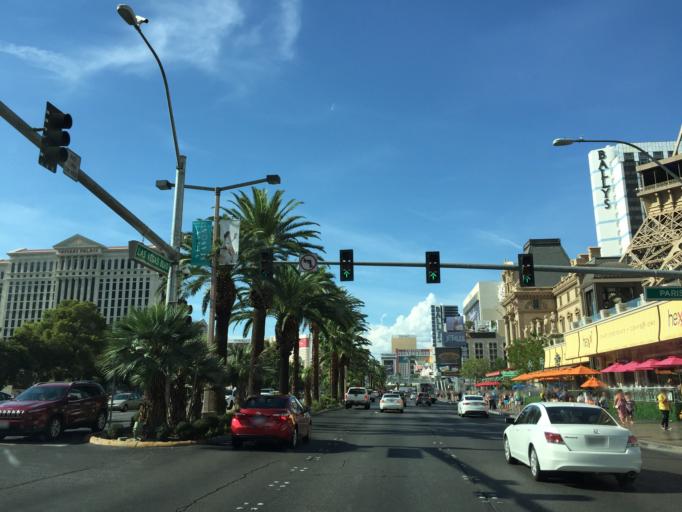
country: US
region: Nevada
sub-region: Clark County
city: Paradise
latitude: 36.1116
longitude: -115.1728
